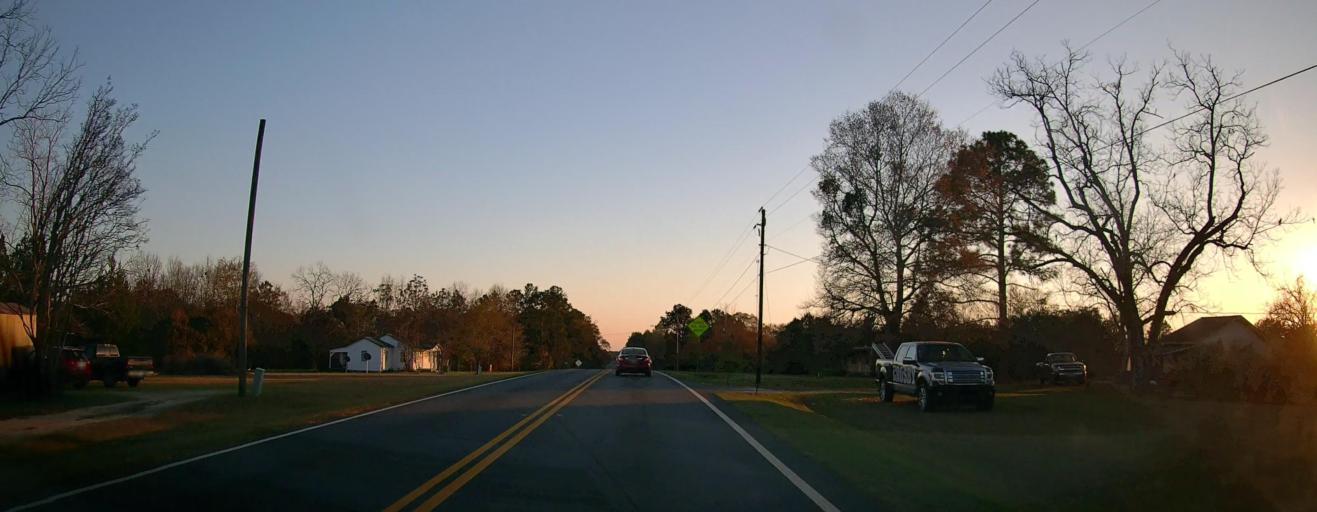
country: US
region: Georgia
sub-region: Dodge County
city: Chester
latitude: 32.3362
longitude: -83.0446
